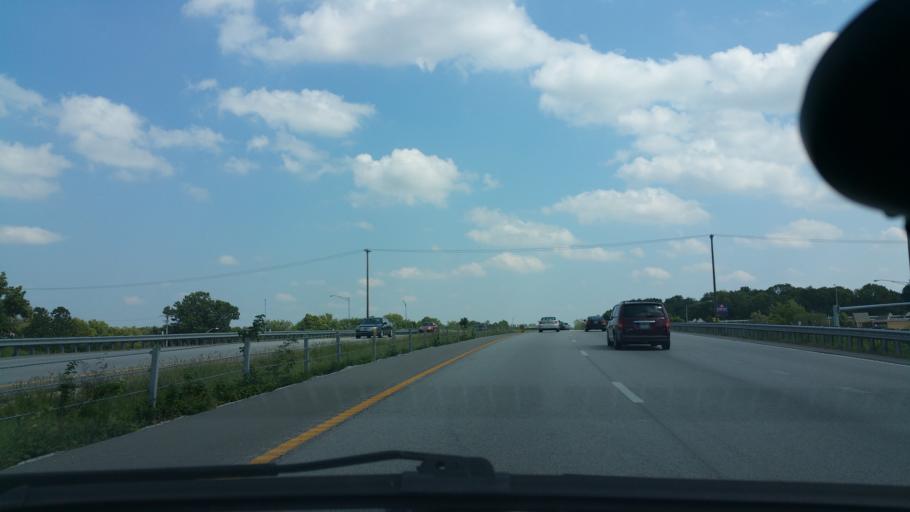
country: US
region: Missouri
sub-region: Clay County
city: Gladstone
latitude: 39.1729
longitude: -94.5508
